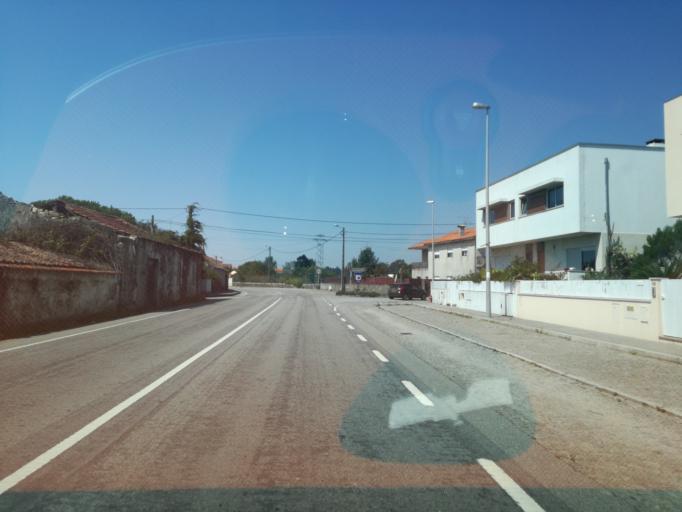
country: PT
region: Braga
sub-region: Esposende
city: Apulia
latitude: 41.4899
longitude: -8.7529
